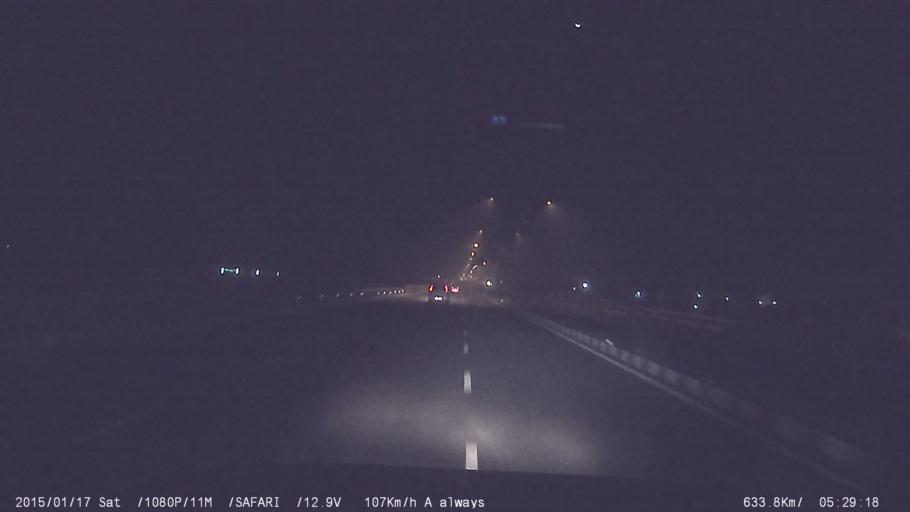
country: IN
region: Tamil Nadu
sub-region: Vellore
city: Arcot
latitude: 12.9169
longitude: 79.2835
